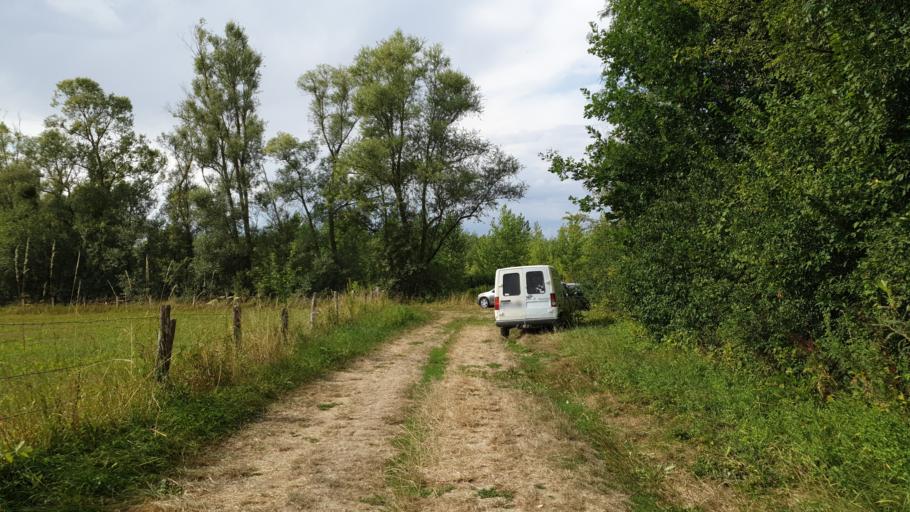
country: FR
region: Champagne-Ardenne
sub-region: Departement de la Marne
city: Pargny-sur-Saulx
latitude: 48.7646
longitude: 4.7481
